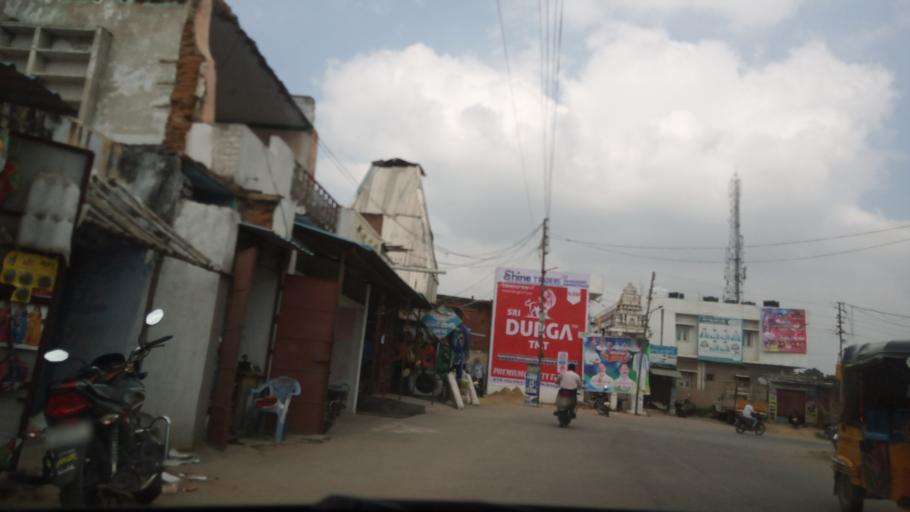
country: IN
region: Andhra Pradesh
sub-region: Chittoor
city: Madanapalle
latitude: 13.6378
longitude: 78.6297
